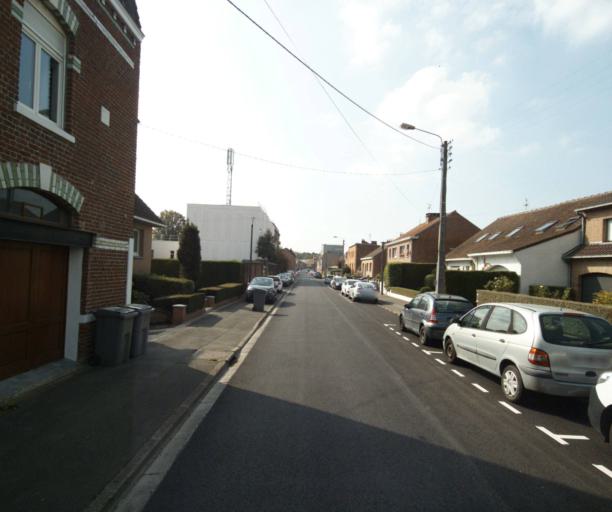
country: FR
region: Nord-Pas-de-Calais
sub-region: Departement du Nord
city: Seclin
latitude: 50.5495
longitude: 3.0276
